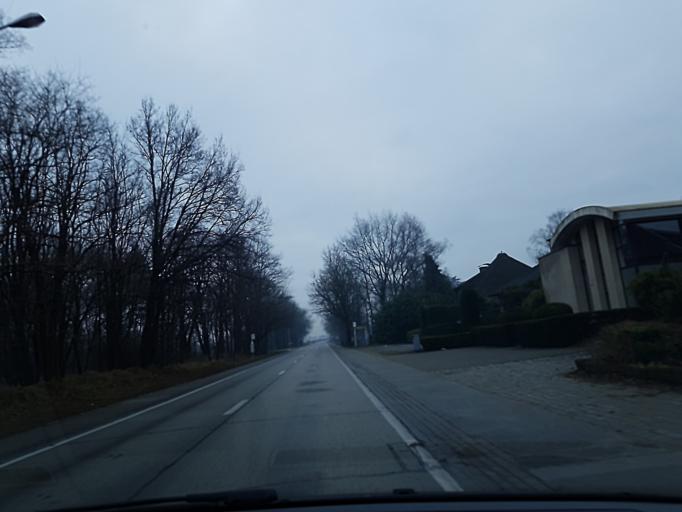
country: BE
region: Flanders
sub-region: Provincie Antwerpen
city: Grobbendonk
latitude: 51.1846
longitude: 4.7425
